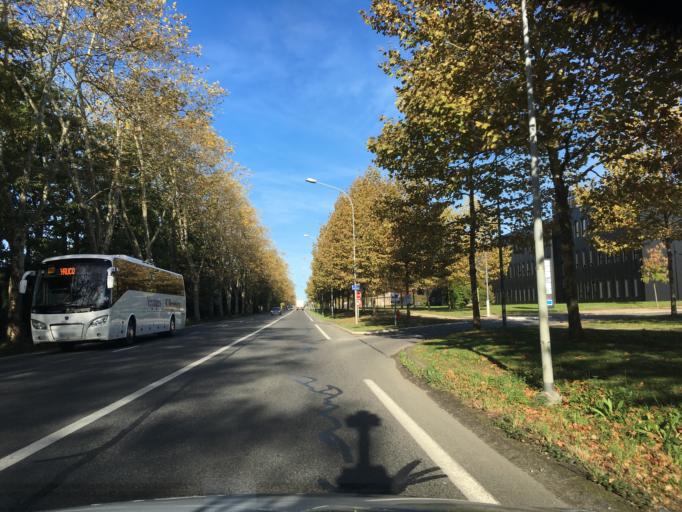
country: FR
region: Aquitaine
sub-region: Departement des Pyrenees-Atlantiques
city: Buros
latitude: 43.3197
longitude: -0.3089
